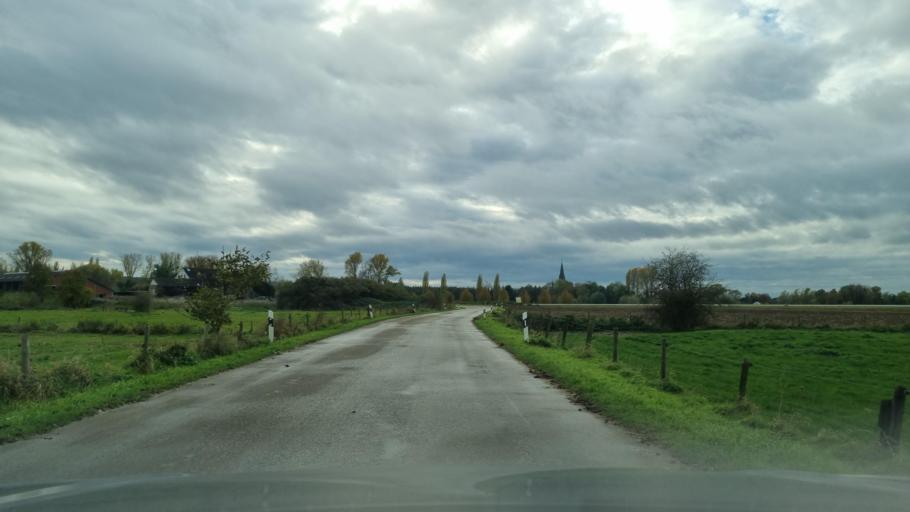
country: DE
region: North Rhine-Westphalia
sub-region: Regierungsbezirk Dusseldorf
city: Kleve
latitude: 51.8170
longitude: 6.1379
